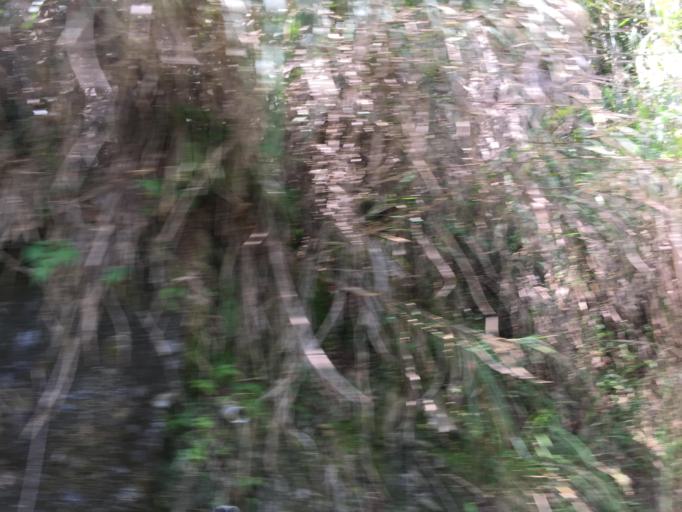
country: TW
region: Taiwan
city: Daxi
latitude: 24.5464
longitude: 121.4013
